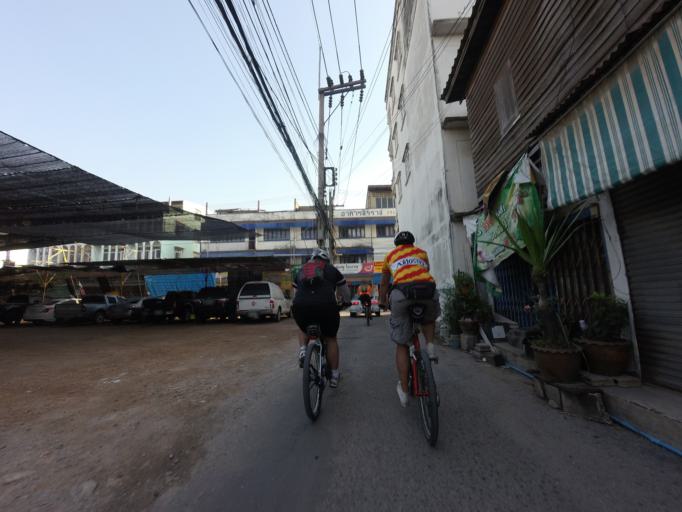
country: TH
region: Samut Sakhon
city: Samut Sakhon
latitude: 13.5469
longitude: 100.2788
